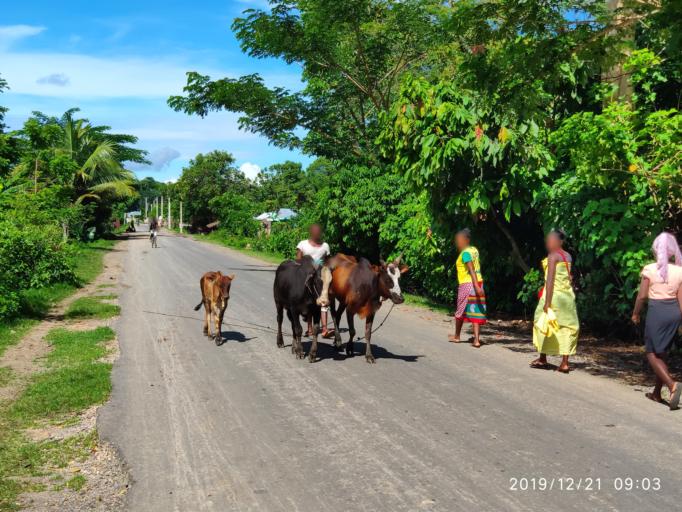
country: MG
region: Diana
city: Ambanja
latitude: -13.6300
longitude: 48.4562
